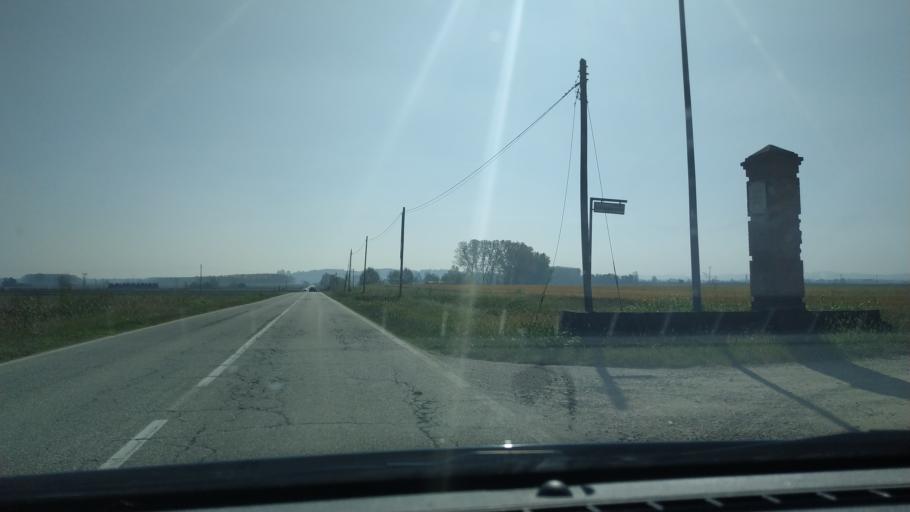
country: IT
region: Piedmont
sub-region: Provincia di Alessandria
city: Ticineto
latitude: 45.0829
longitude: 8.5593
